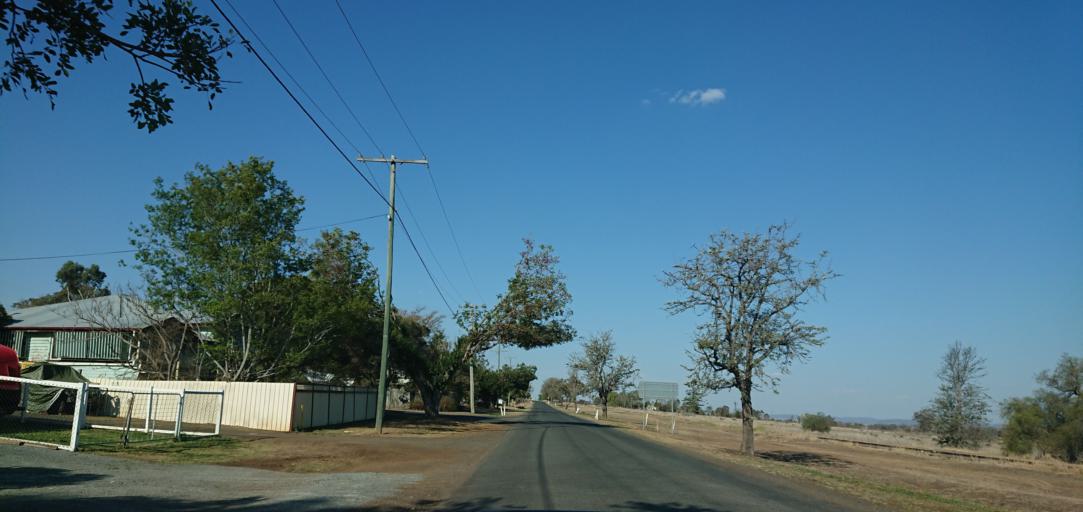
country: AU
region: Queensland
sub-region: Toowoomba
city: Westbrook
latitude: -27.6784
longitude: 151.7150
